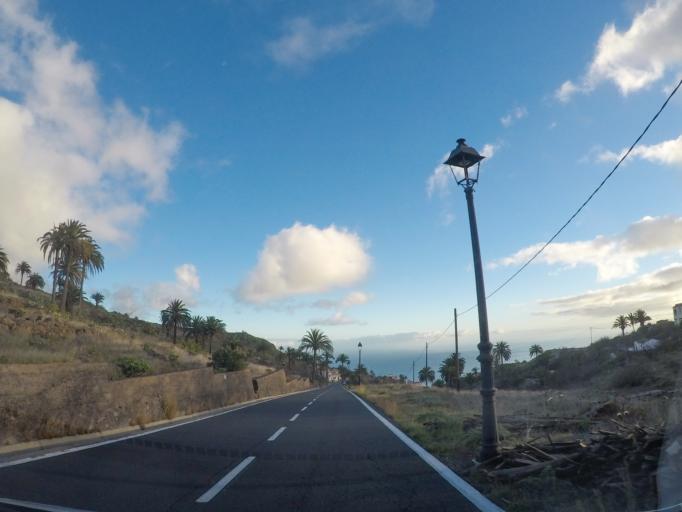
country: ES
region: Canary Islands
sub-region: Provincia de Santa Cruz de Tenerife
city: Alajero
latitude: 28.0675
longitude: -17.2385
